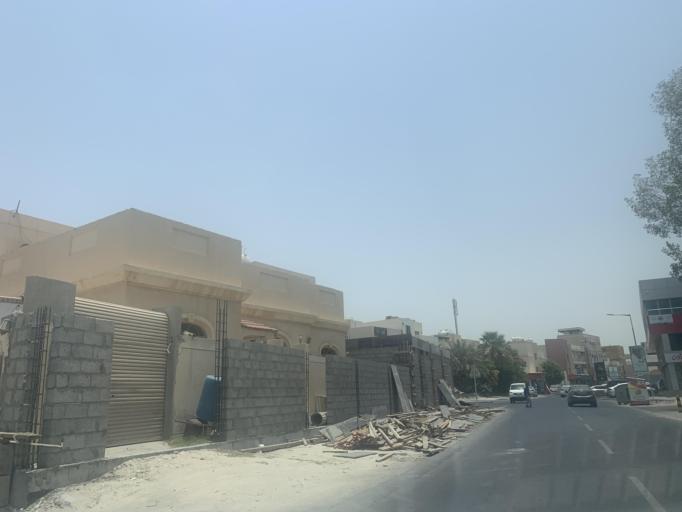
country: BH
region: Manama
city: Jidd Hafs
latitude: 26.2185
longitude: 50.4587
